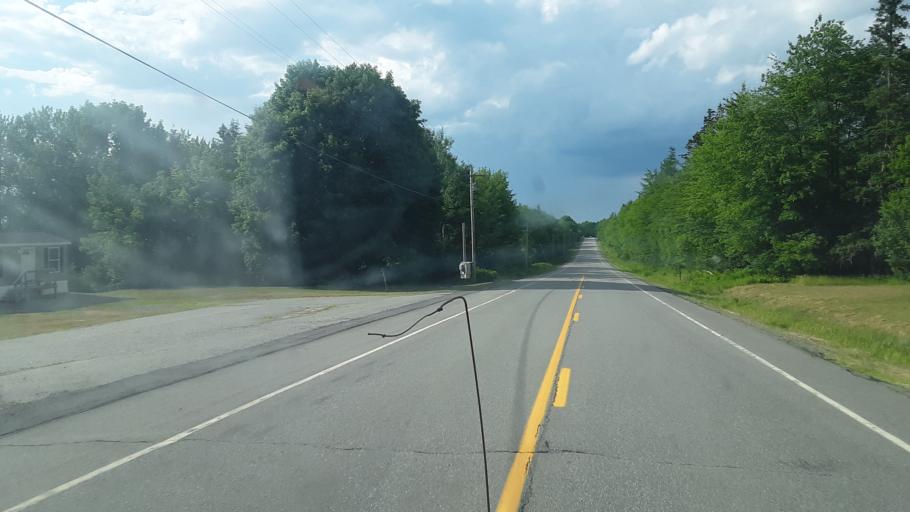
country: US
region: Maine
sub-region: Washington County
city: Machias
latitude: 45.0049
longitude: -67.5530
